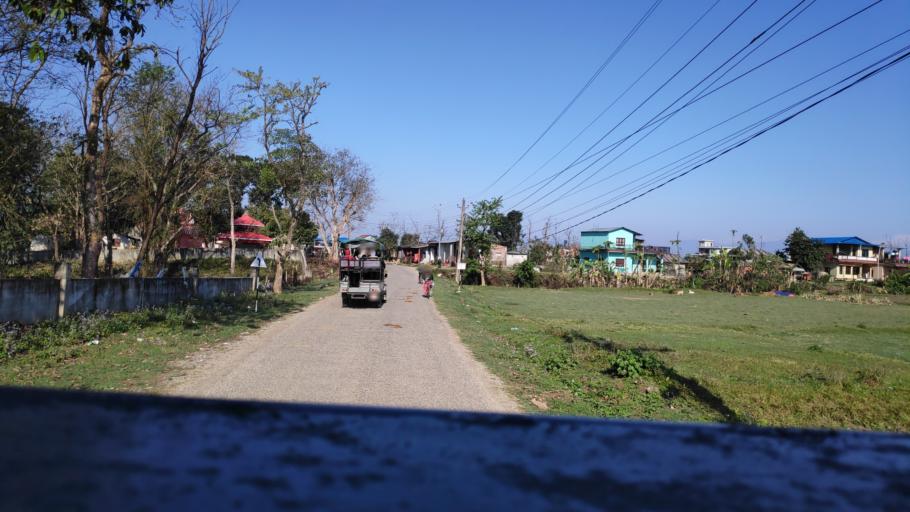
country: NP
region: Central Region
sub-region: Narayani Zone
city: Bharatpur
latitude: 27.5757
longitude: 84.5062
